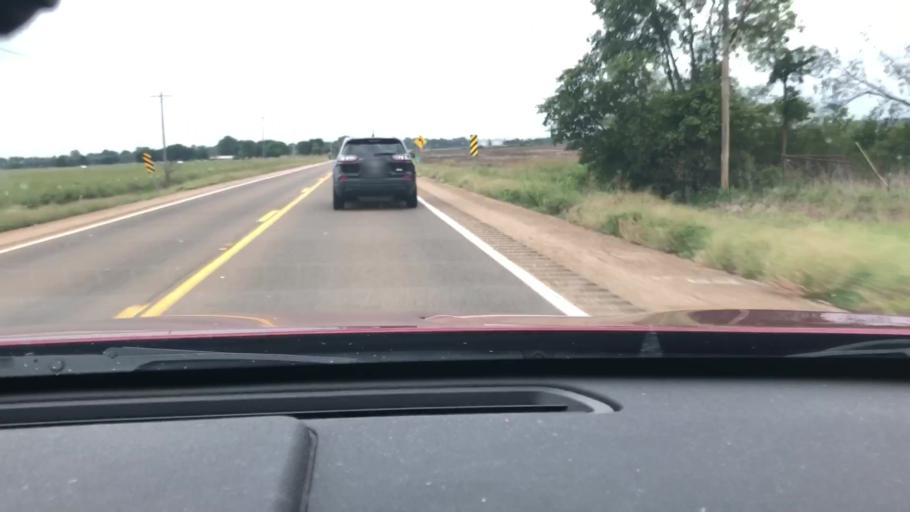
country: US
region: Arkansas
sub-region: Lafayette County
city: Lewisville
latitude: 33.3808
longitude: -93.7366
